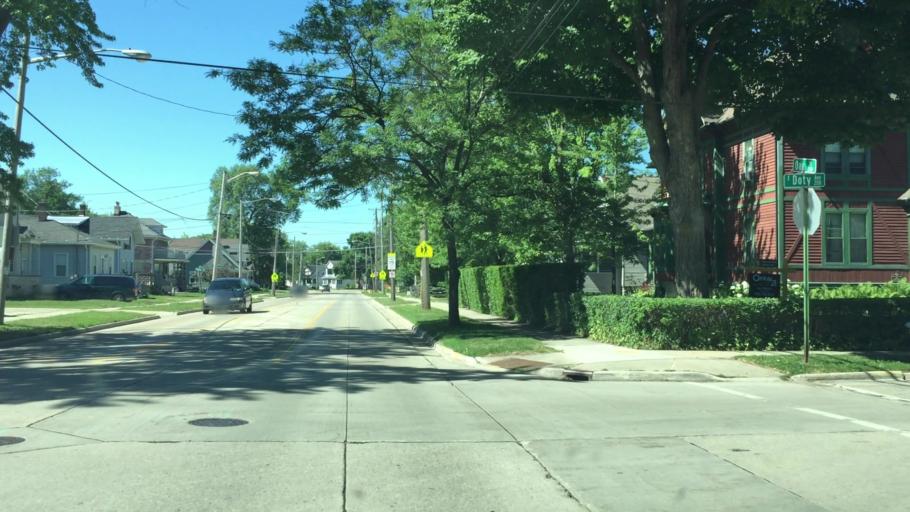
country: US
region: Wisconsin
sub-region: Winnebago County
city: Neenah
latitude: 44.1837
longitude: -88.4581
